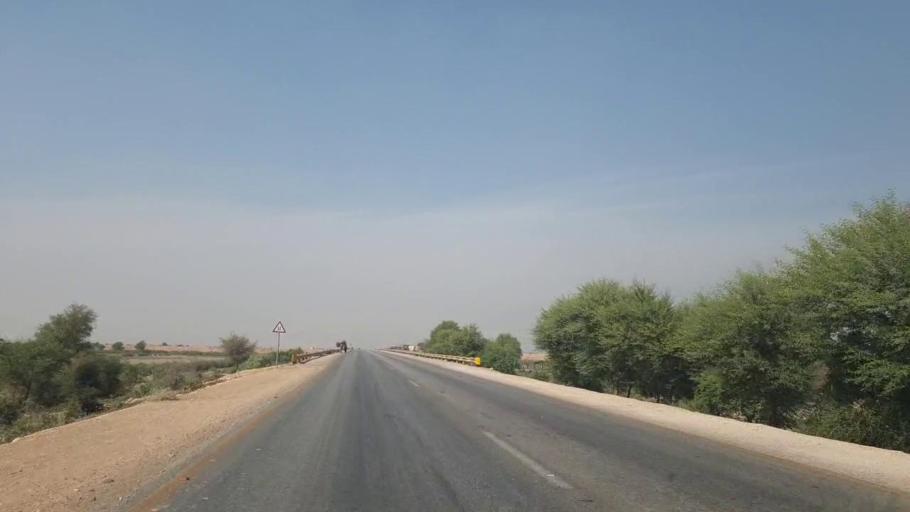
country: PK
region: Sindh
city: Hala
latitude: 25.8778
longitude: 68.2499
